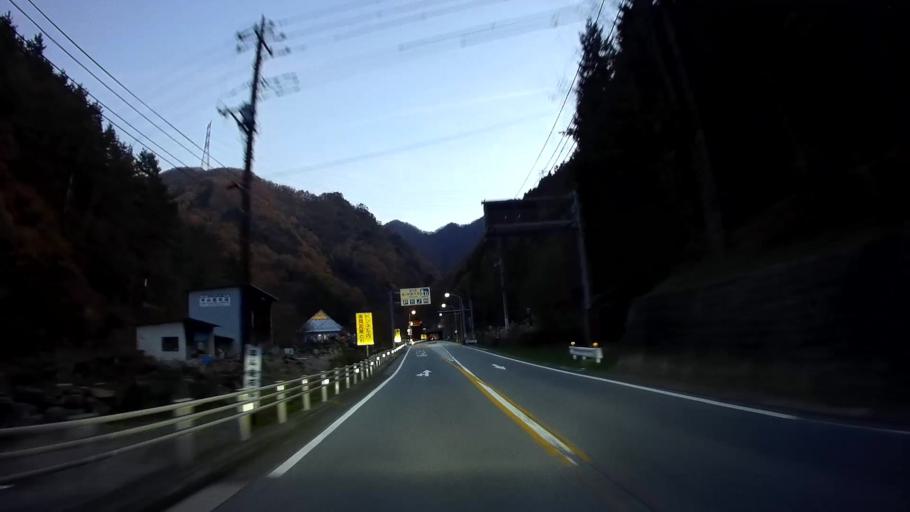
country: JP
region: Yamanashi
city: Enzan
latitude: 35.6374
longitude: 138.7919
